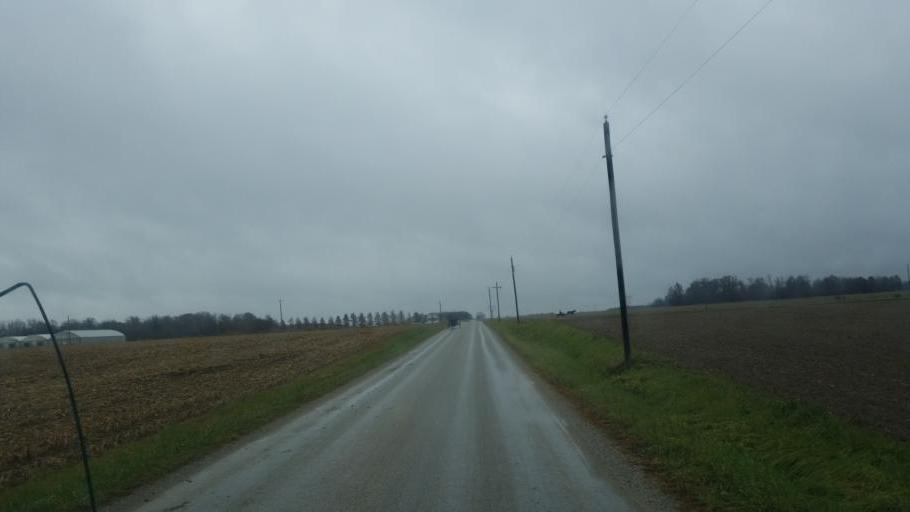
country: US
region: Indiana
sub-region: Adams County
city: Berne
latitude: 40.6966
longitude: -84.9173
